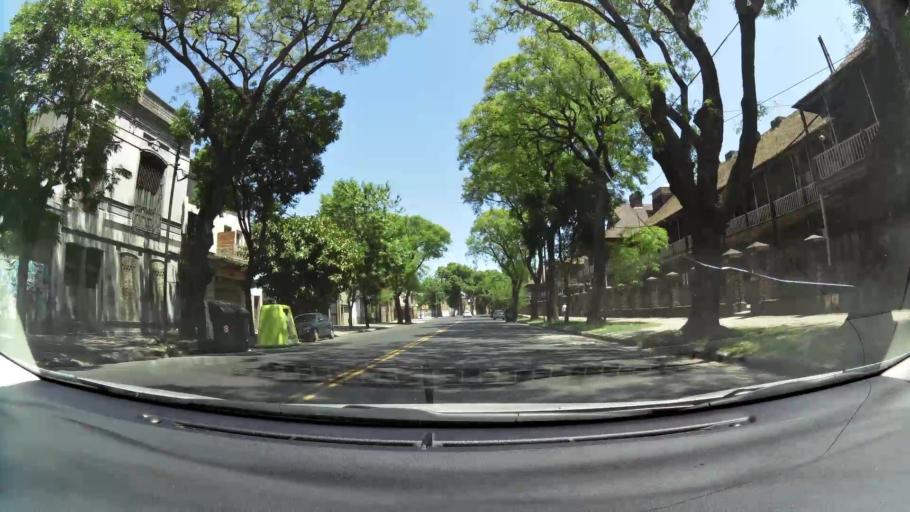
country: AR
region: Buenos Aires
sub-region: Partido de Avellaneda
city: Avellaneda
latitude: -34.6464
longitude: -58.3853
